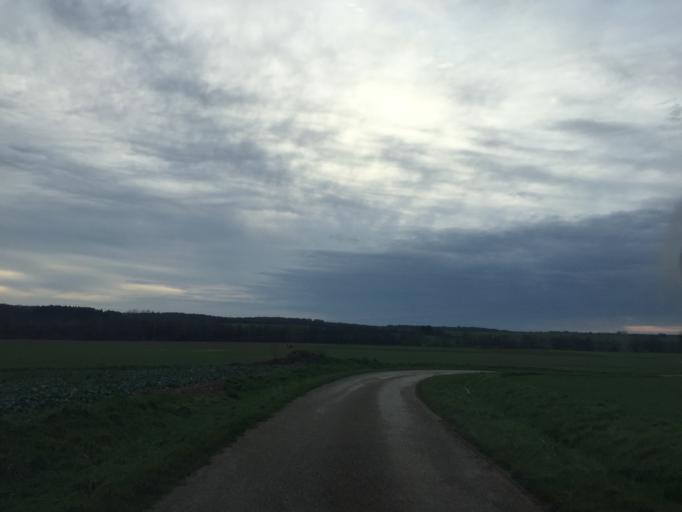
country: FR
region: Franche-Comte
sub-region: Departement du Jura
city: Mont-sous-Vaudrey
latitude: 46.9390
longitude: 5.6812
